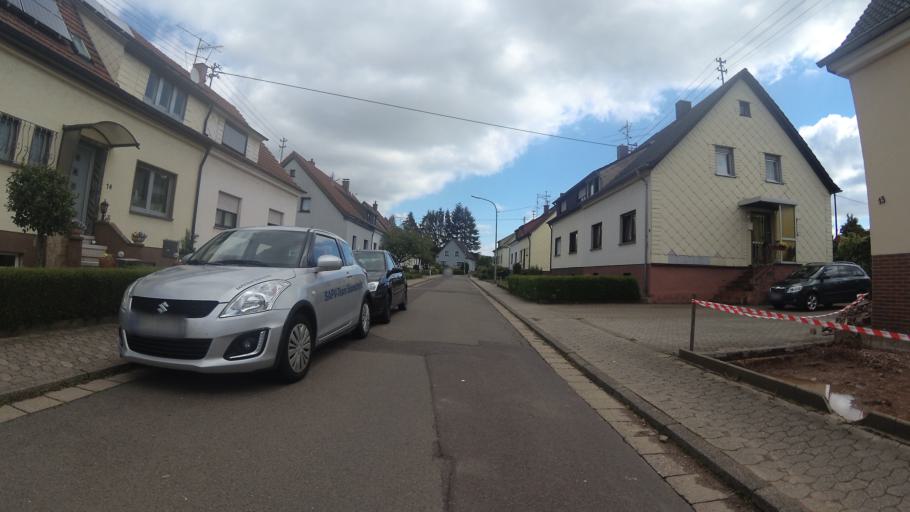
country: DE
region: Saarland
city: Lebach
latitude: 49.4042
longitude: 6.9041
